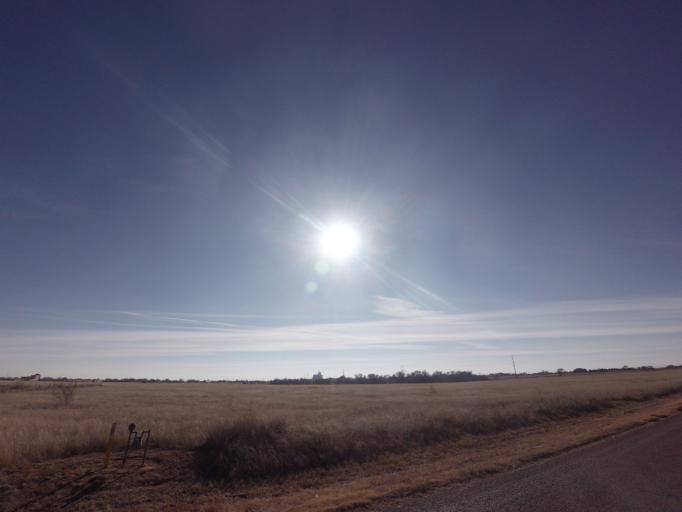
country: US
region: New Mexico
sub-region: Curry County
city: Clovis
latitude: 34.4192
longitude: -103.2453
